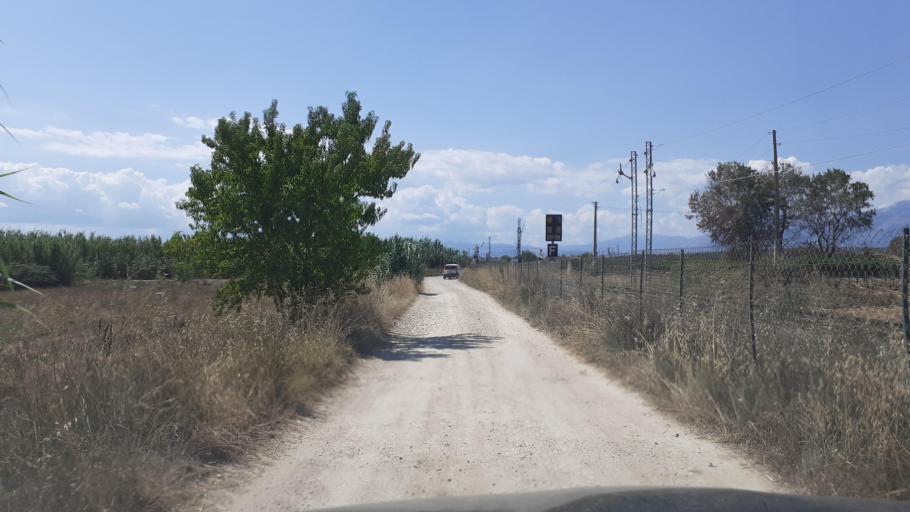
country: IT
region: Abruzzo
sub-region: Provincia di Chieti
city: Fossacesia
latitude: 42.2039
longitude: 14.4903
